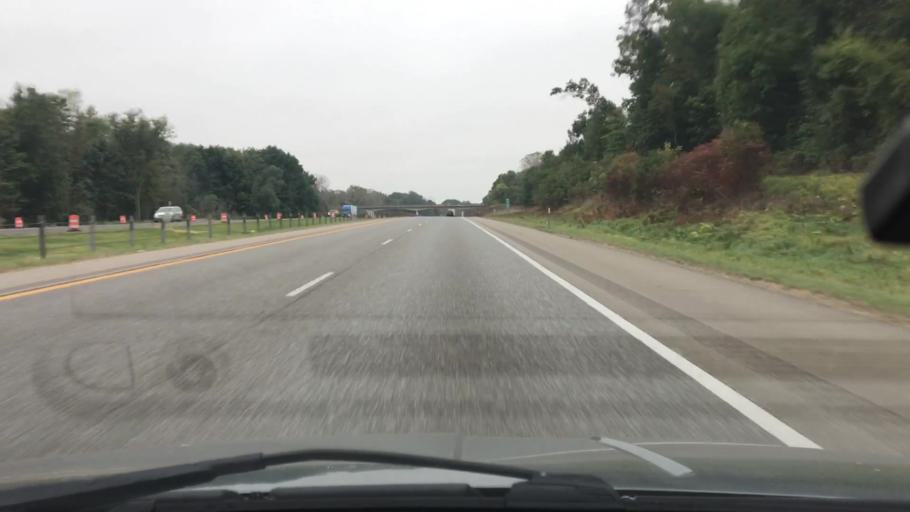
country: US
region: Michigan
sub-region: Van Buren County
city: Decatur
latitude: 42.1929
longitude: -85.9886
